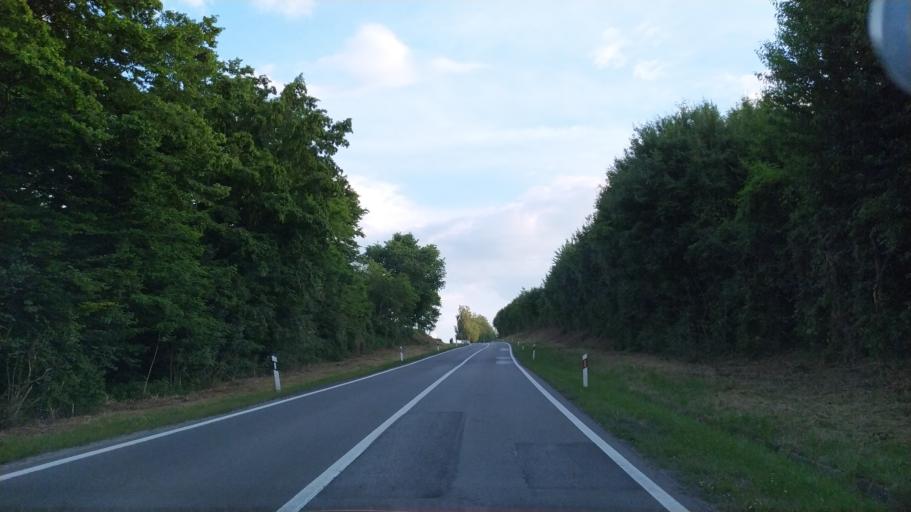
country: HR
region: Osjecko-Baranjska
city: Fericanci
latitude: 45.5062
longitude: 18.0135
